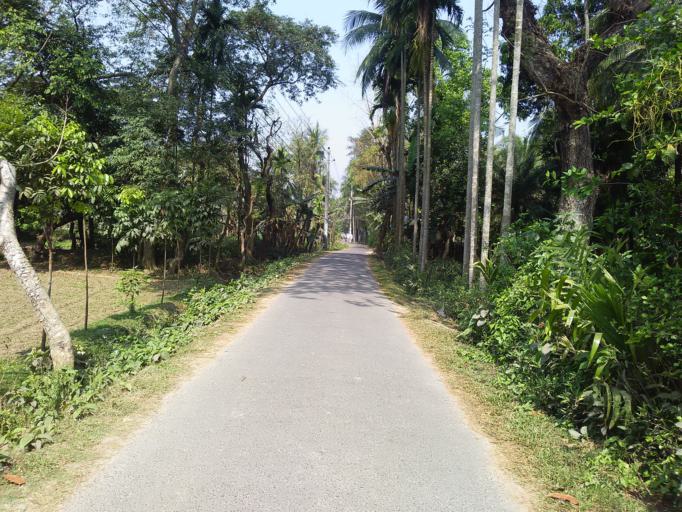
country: BD
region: Khulna
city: Khulna
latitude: 22.8770
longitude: 89.5428
